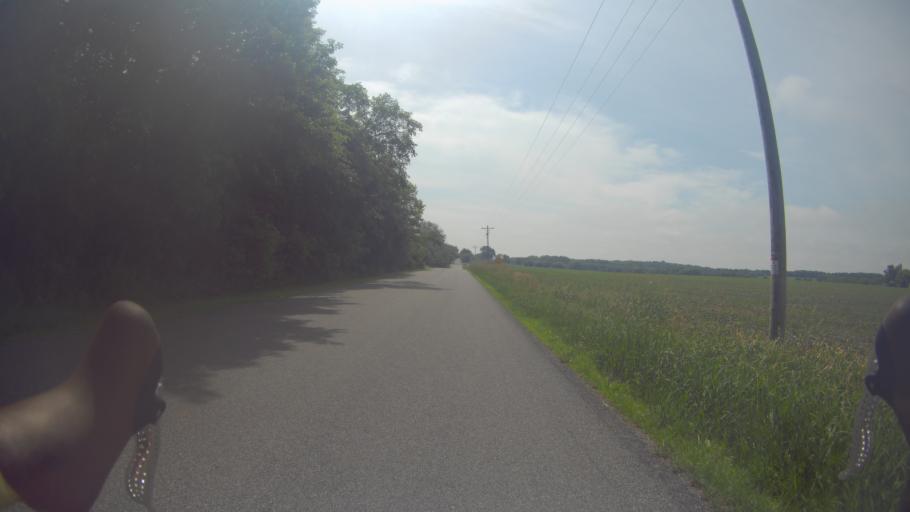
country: US
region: Wisconsin
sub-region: Rock County
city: Edgerton
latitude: 42.8574
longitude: -89.0431
